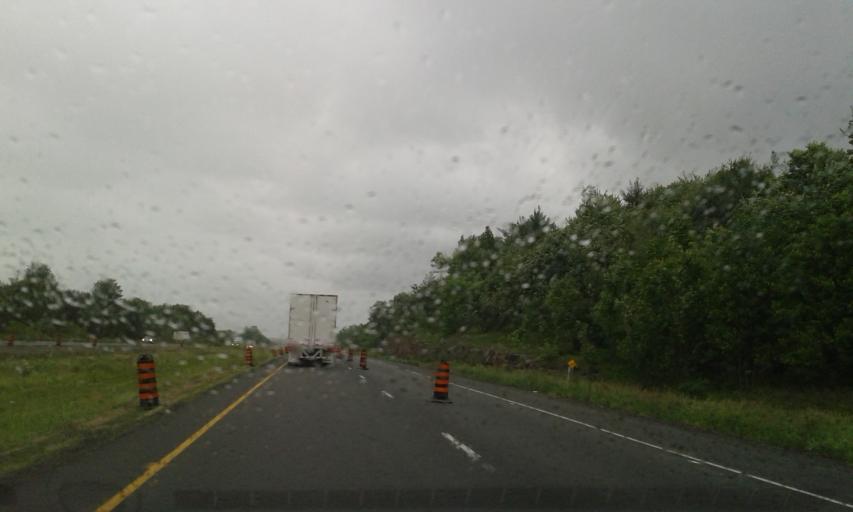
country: CA
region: Ontario
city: Gananoque
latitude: 44.3671
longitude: -76.0652
